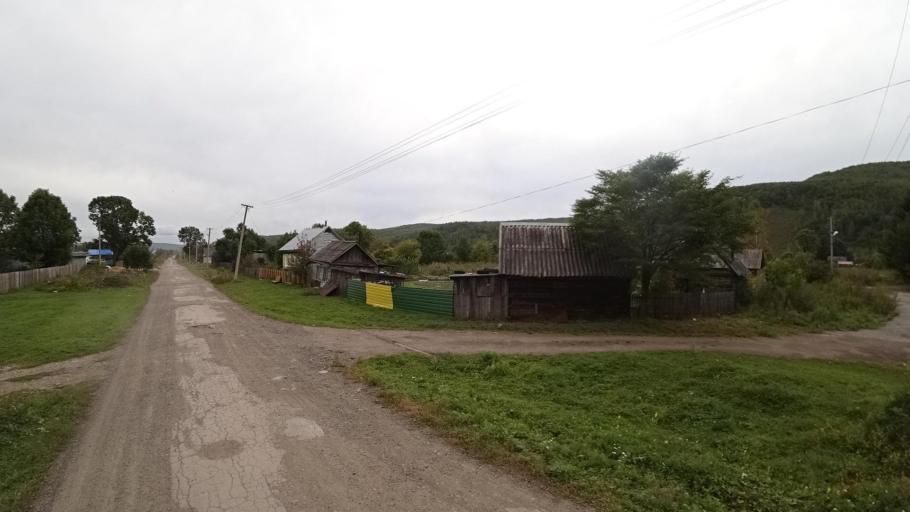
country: RU
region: Jewish Autonomous Oblast
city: Khingansk
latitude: 49.0393
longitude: 131.0497
